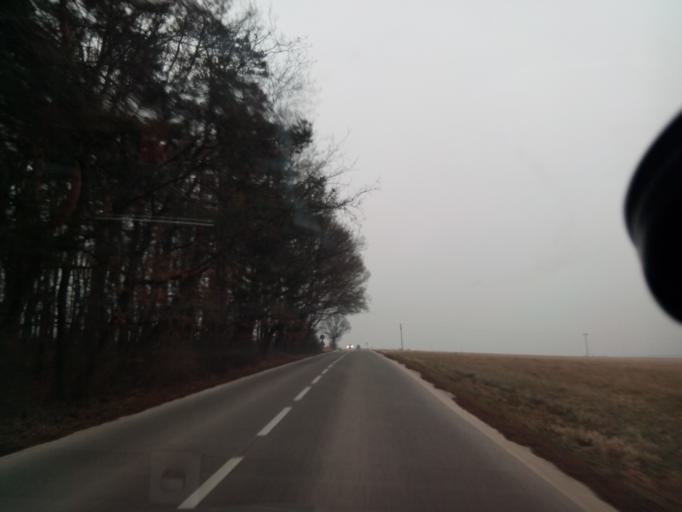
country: SK
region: Kosicky
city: Moldava nad Bodvou
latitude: 48.6782
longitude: 21.0838
